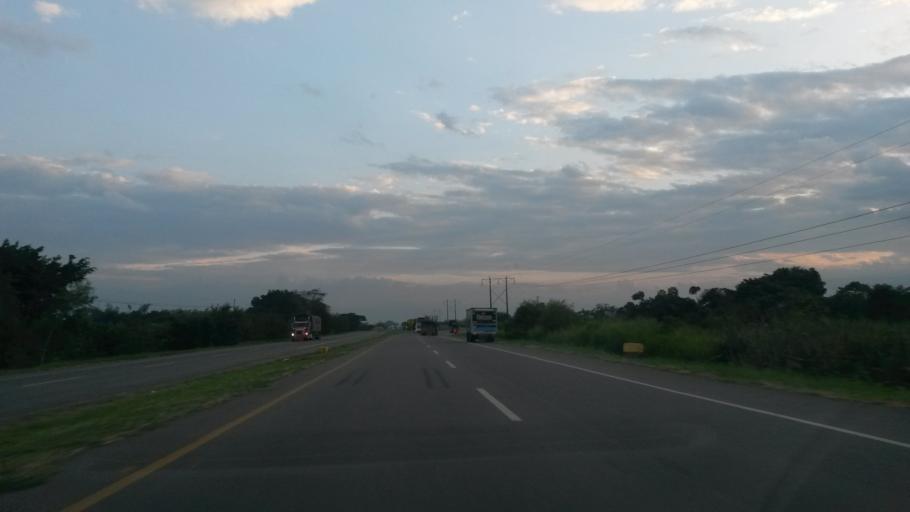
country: CO
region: Cauca
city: Santander de Quilichao
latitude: 3.0921
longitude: -76.4705
